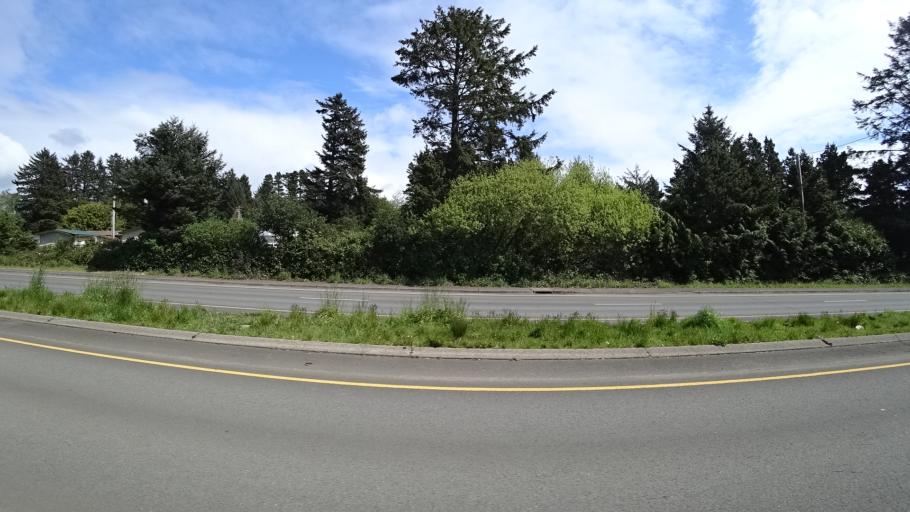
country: US
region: Oregon
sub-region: Lincoln County
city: Lincoln Beach
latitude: 44.8547
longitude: -124.0418
